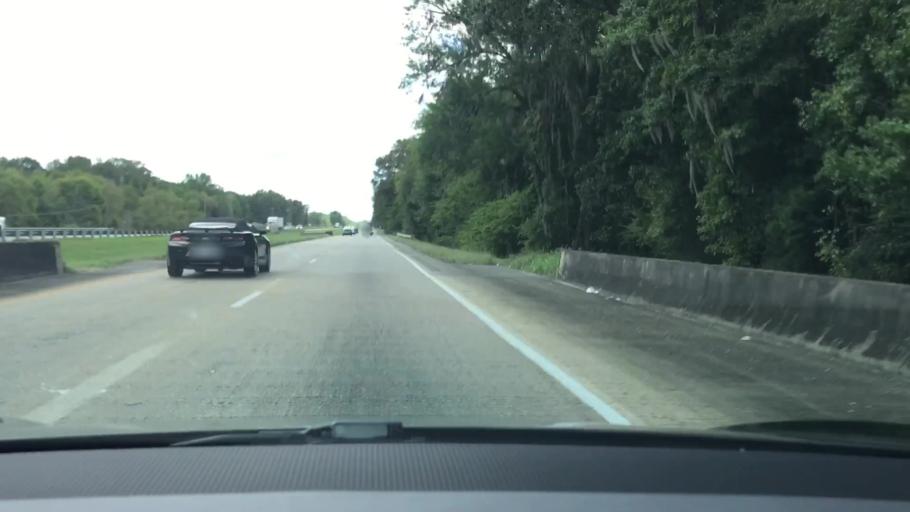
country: US
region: Alabama
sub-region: Montgomery County
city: Pike Road
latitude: 32.1842
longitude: -86.1175
